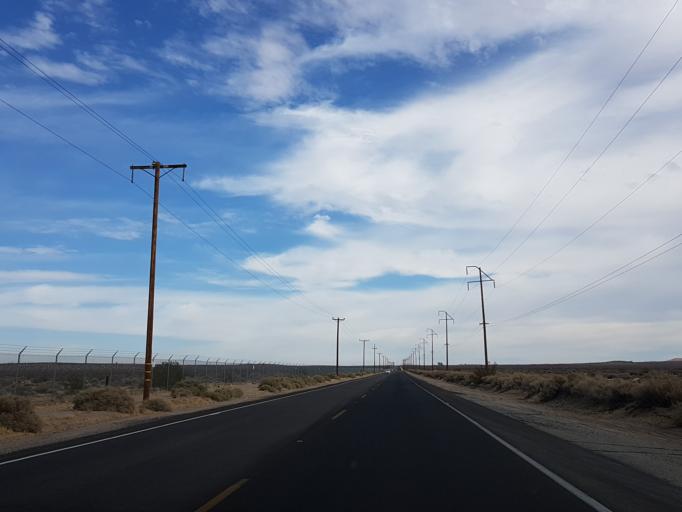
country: US
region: California
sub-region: Kern County
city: Ridgecrest
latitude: 35.6226
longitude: -117.6255
